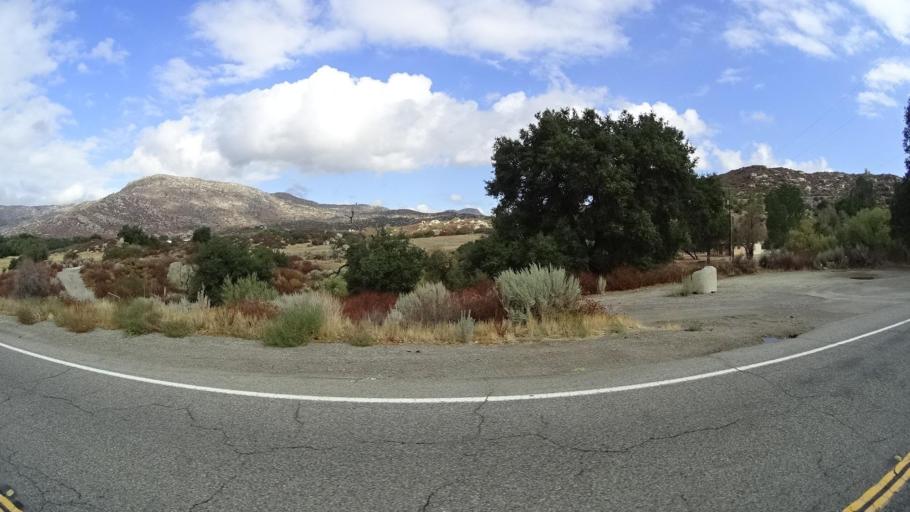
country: US
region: California
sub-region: San Diego County
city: Campo
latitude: 32.5987
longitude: -116.4975
